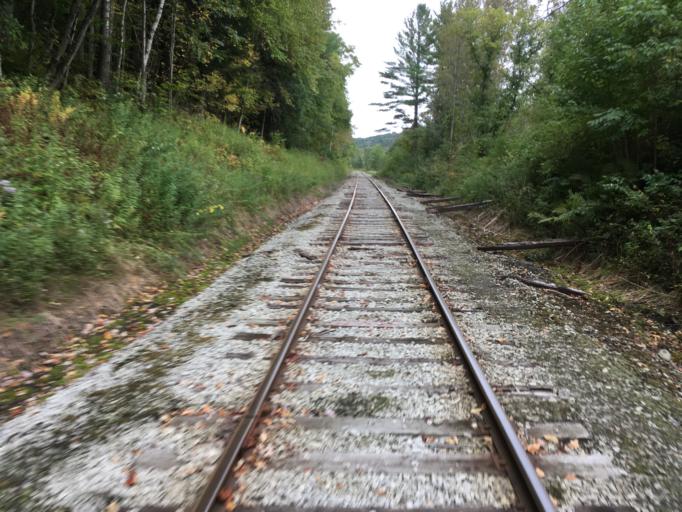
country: US
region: Vermont
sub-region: Washington County
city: Montpelier
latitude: 44.2353
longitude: -72.5502
